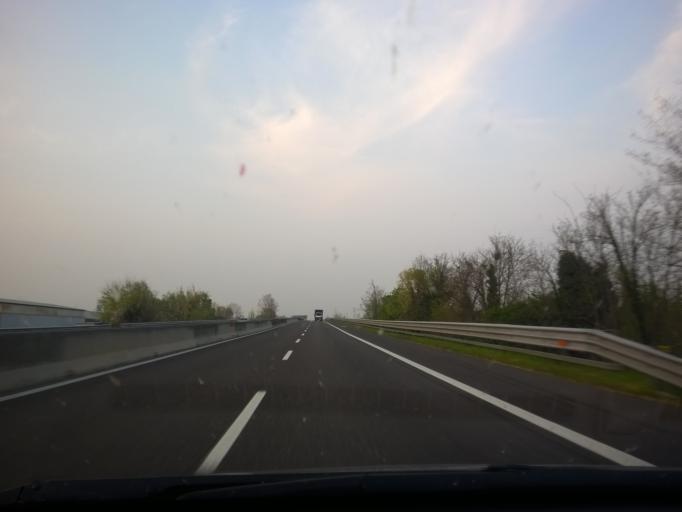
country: IT
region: Veneto
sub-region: Provincia di Padova
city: Villatora
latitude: 45.3969
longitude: 11.9604
